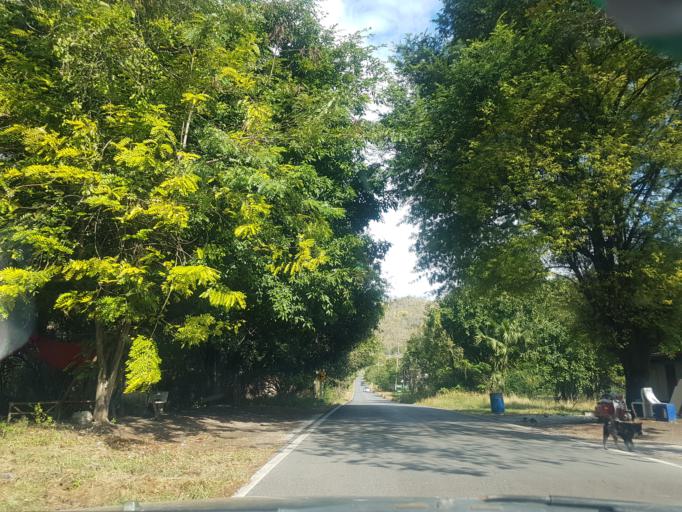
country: TH
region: Lop Buri
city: Lop Buri
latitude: 14.8184
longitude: 100.7510
